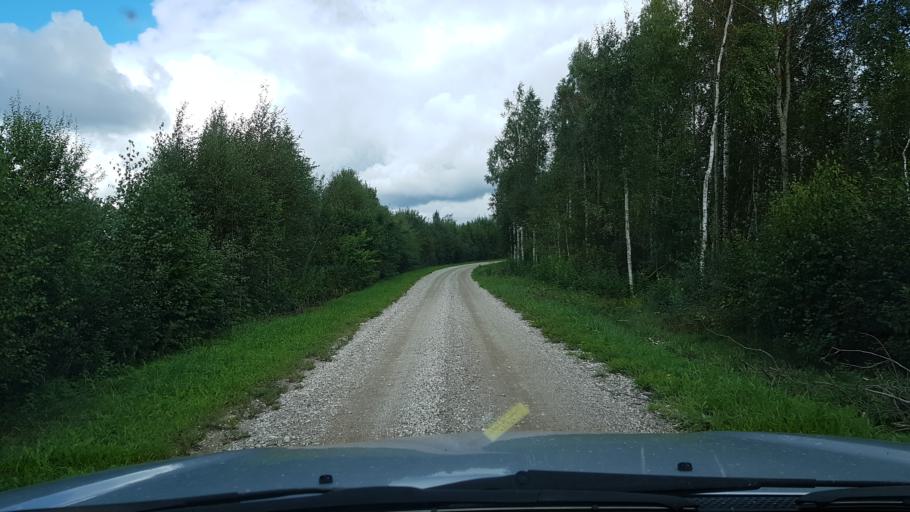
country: EE
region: Harju
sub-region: Rae vald
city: Vaida
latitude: 59.2682
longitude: 25.0480
